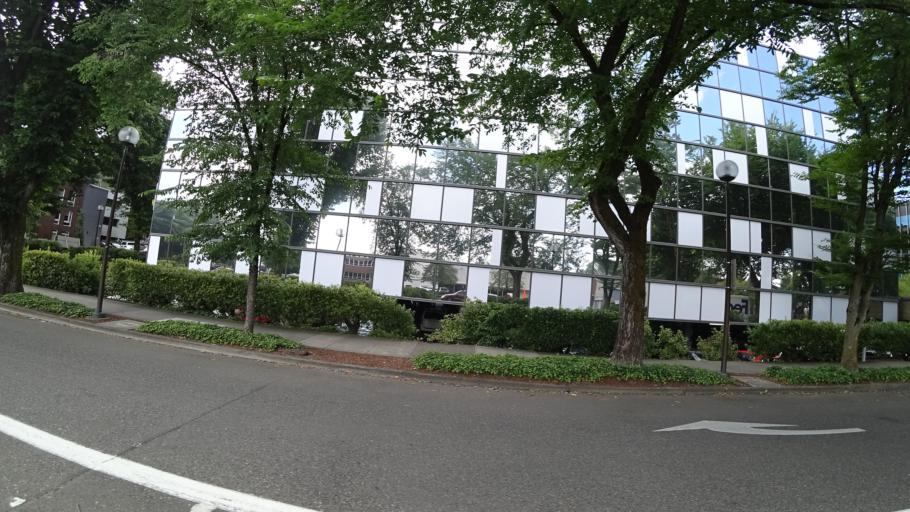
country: US
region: Oregon
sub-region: Multnomah County
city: Portland
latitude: 45.5042
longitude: -122.6788
